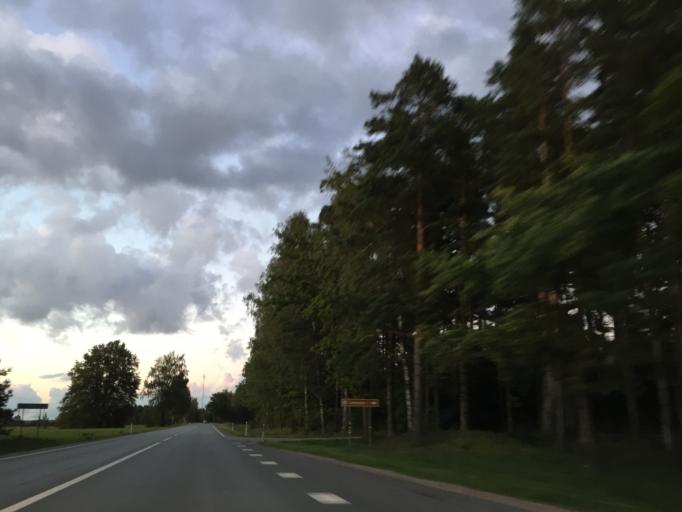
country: LV
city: Tireli
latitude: 56.8732
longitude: 23.6260
